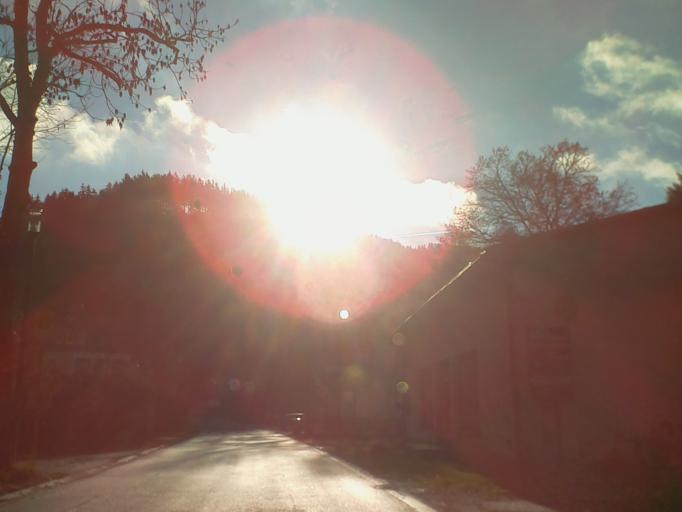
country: DE
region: Thuringia
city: Meuselbach
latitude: 50.5838
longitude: 11.0778
